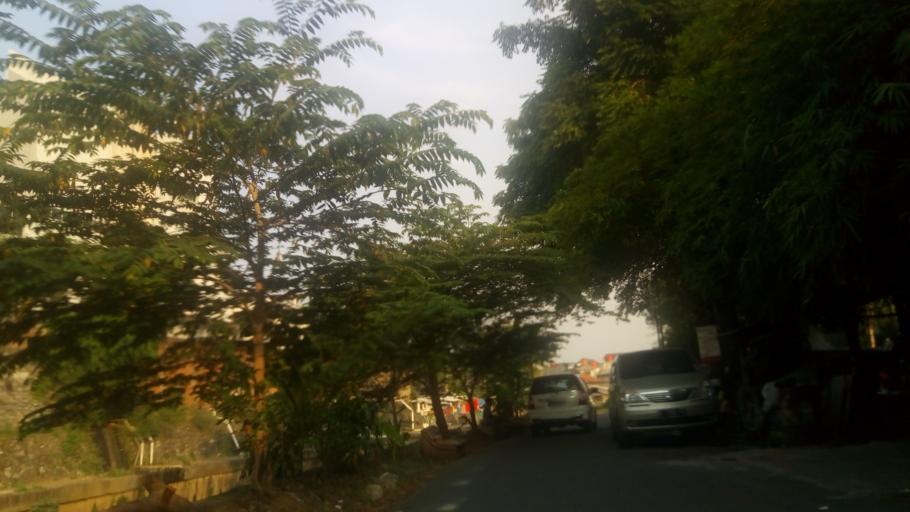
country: ID
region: Jakarta Raya
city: Jakarta
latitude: -6.2028
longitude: 106.8553
